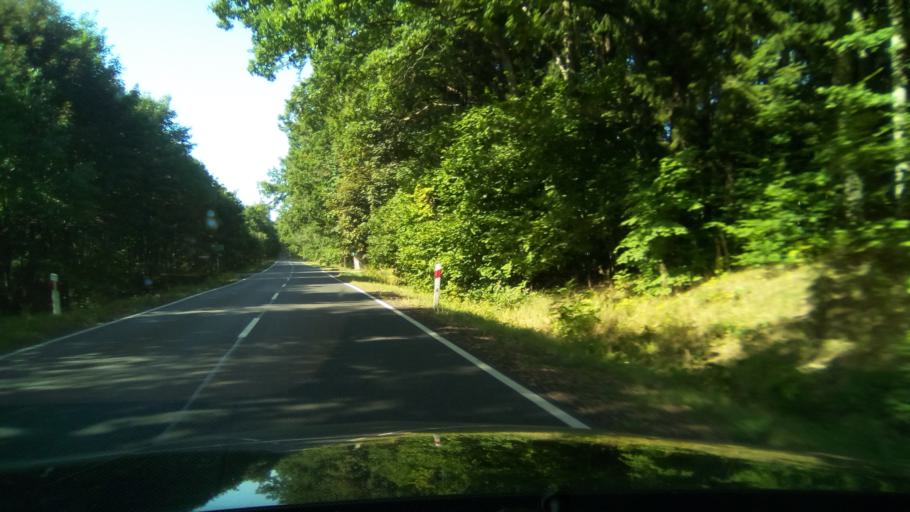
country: PL
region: West Pomeranian Voivodeship
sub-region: Powiat swidwinski
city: Polczyn-Zdroj
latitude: 53.7642
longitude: 16.1874
